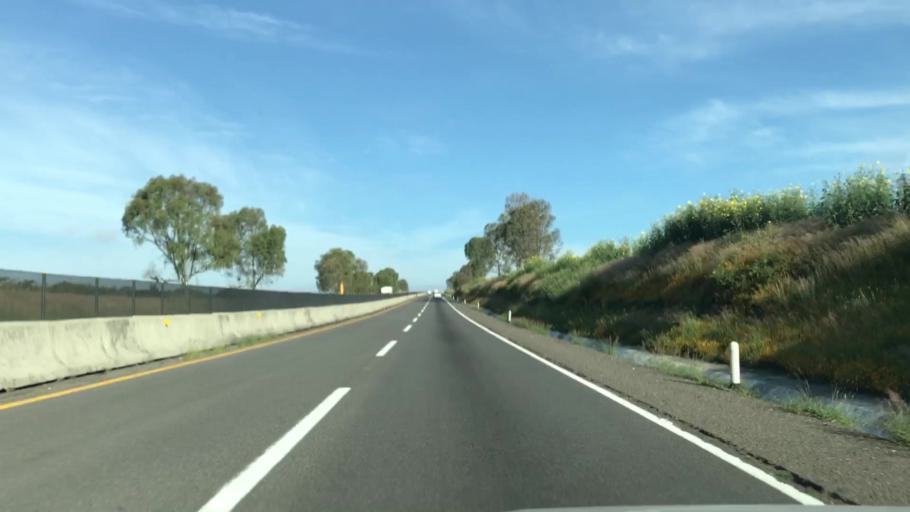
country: MX
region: Jalisco
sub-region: Lagos de Moreno
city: Cristeros [Fraccionamiento]
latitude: 21.3669
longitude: -102.1270
